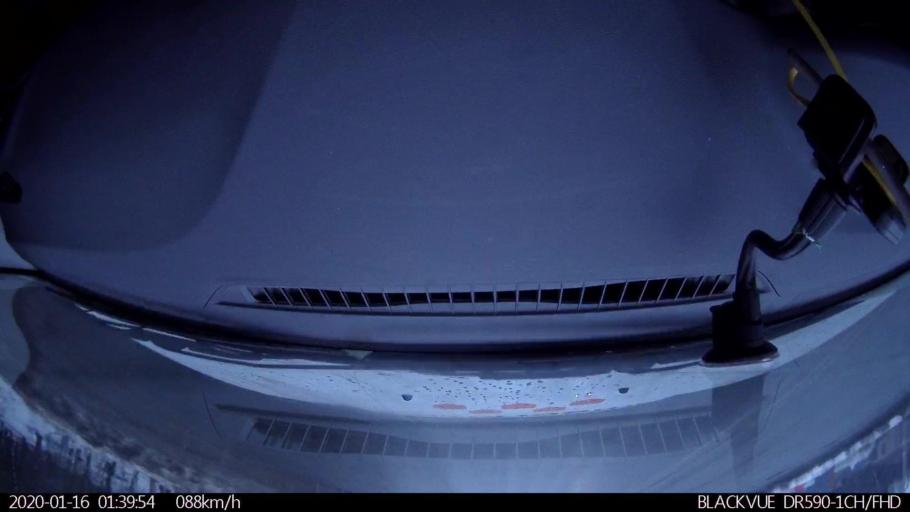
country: RU
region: Nizjnij Novgorod
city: Gorbatovka
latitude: 56.3310
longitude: 43.7878
